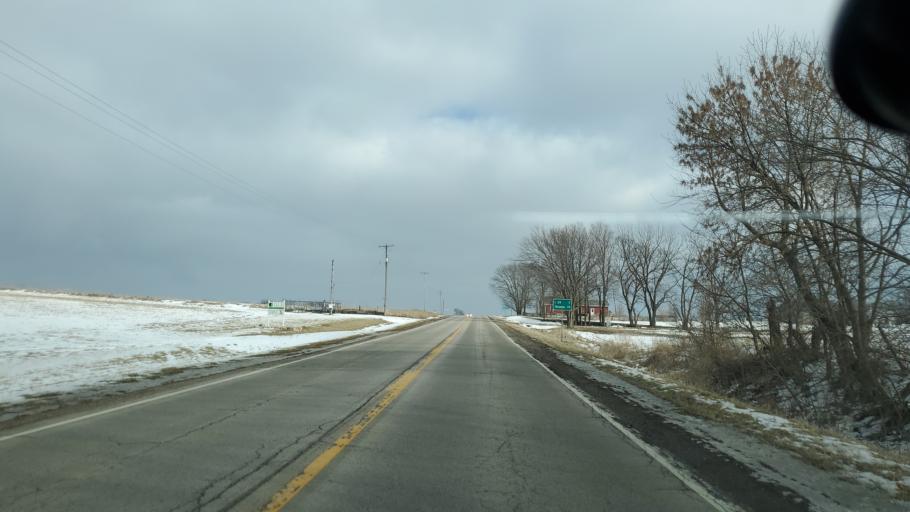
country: US
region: Illinois
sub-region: Marshall County
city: Toluca
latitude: 41.1185
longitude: -89.1977
